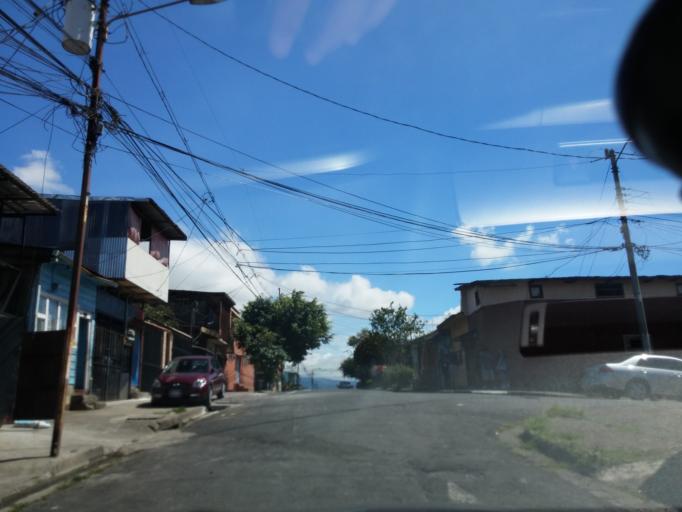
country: CR
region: San Jose
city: San Jose
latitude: 9.9210
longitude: -84.0865
